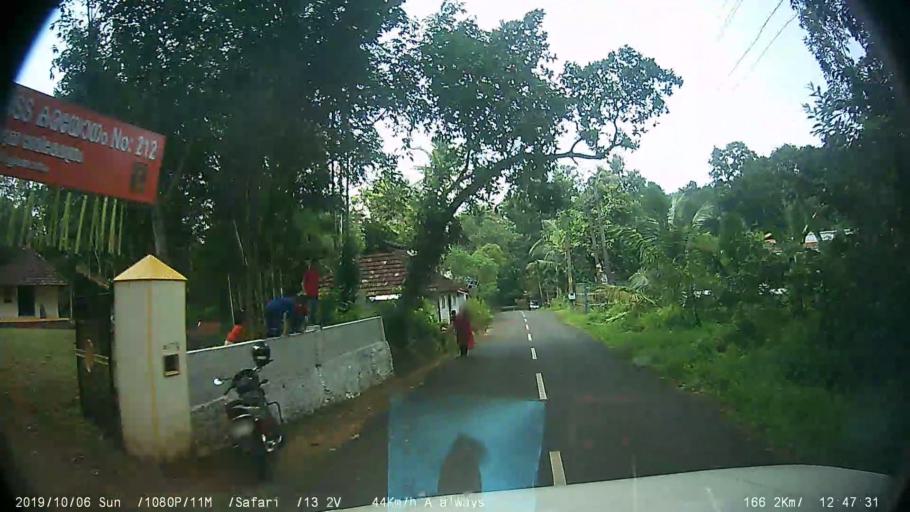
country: IN
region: Kerala
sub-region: Kottayam
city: Palackattumala
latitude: 9.7751
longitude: 76.6015
